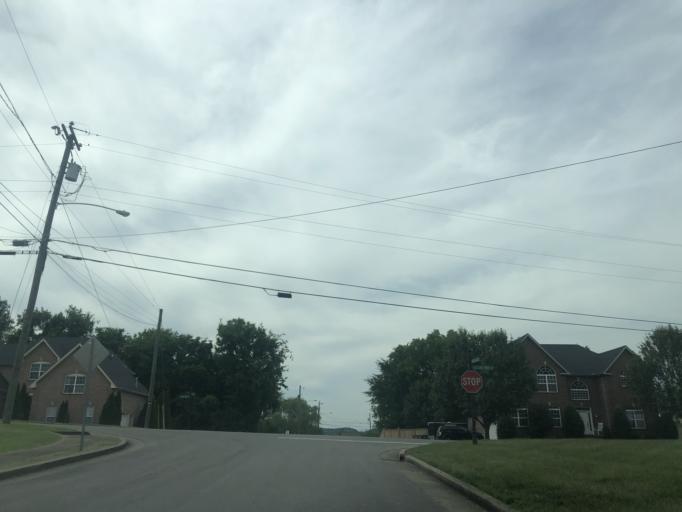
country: US
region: Tennessee
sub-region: Davidson County
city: Nashville
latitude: 36.2100
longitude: -86.8117
